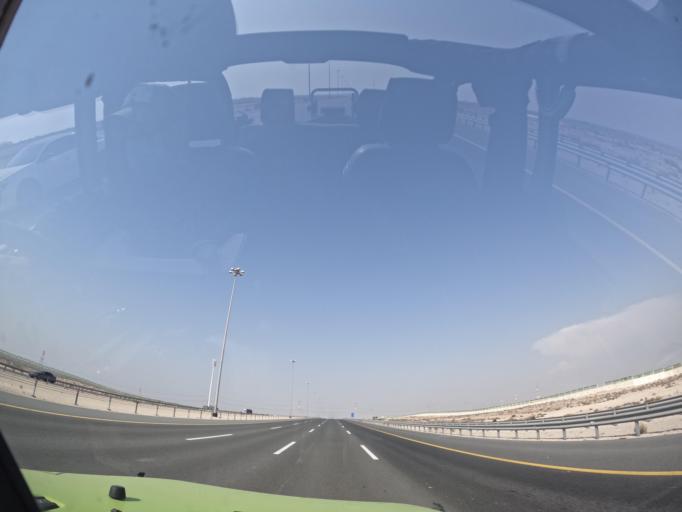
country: AE
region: Abu Dhabi
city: Abu Dhabi
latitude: 24.6402
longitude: 54.7850
